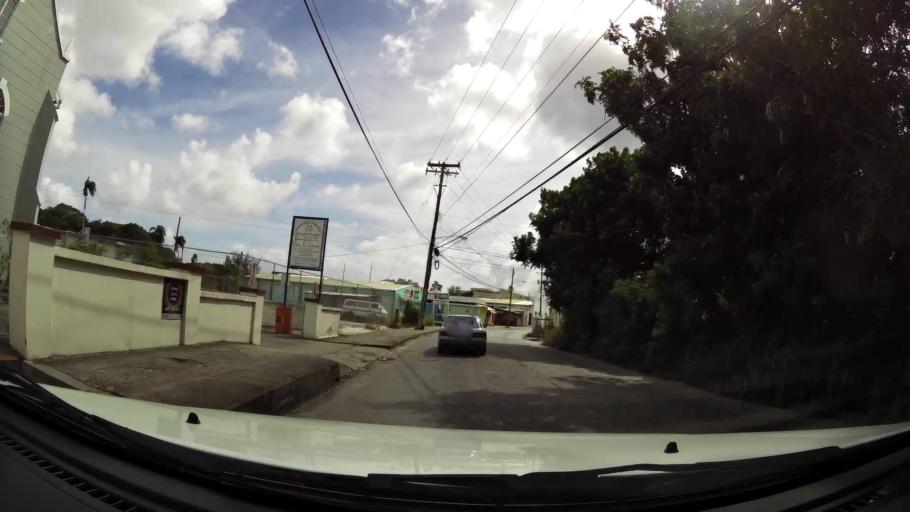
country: BB
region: Saint Michael
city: Bridgetown
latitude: 13.1051
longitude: -59.6133
